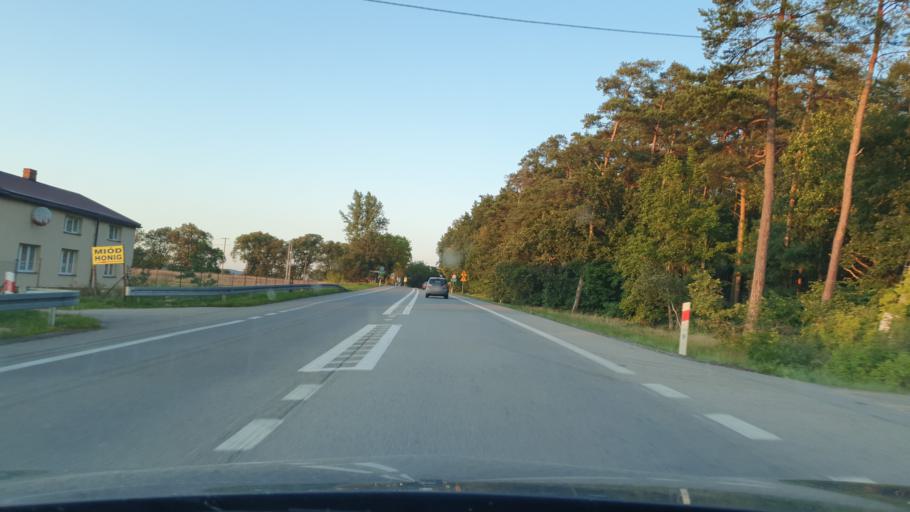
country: PL
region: Pomeranian Voivodeship
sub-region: Powiat leborski
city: Nowa Wies Leborska
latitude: 54.5096
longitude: 17.6684
